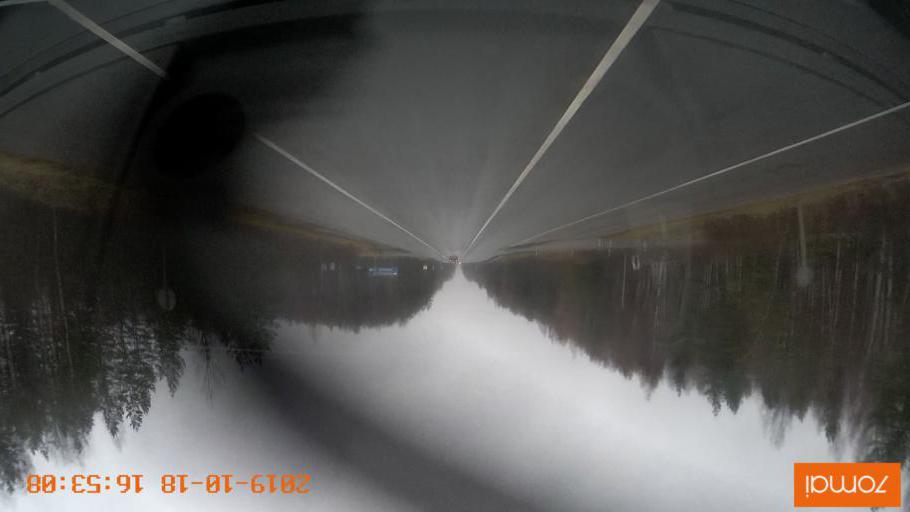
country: RU
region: Ivanovo
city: Nerl'
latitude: 56.6107
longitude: 40.5574
